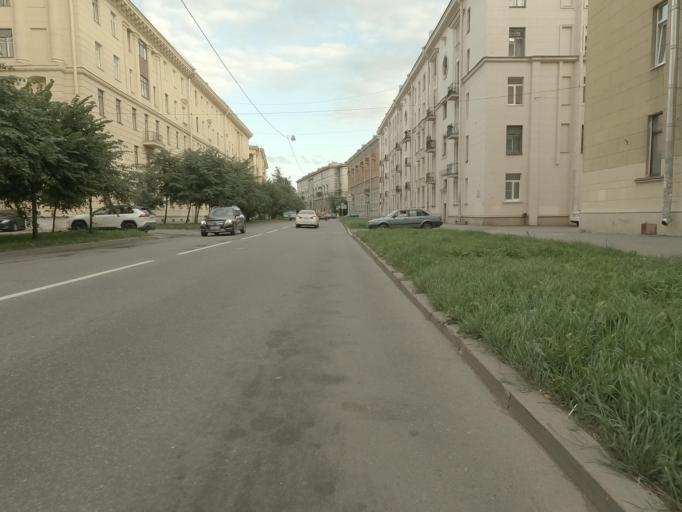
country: RU
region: St.-Petersburg
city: Avtovo
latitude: 59.8701
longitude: 30.2641
